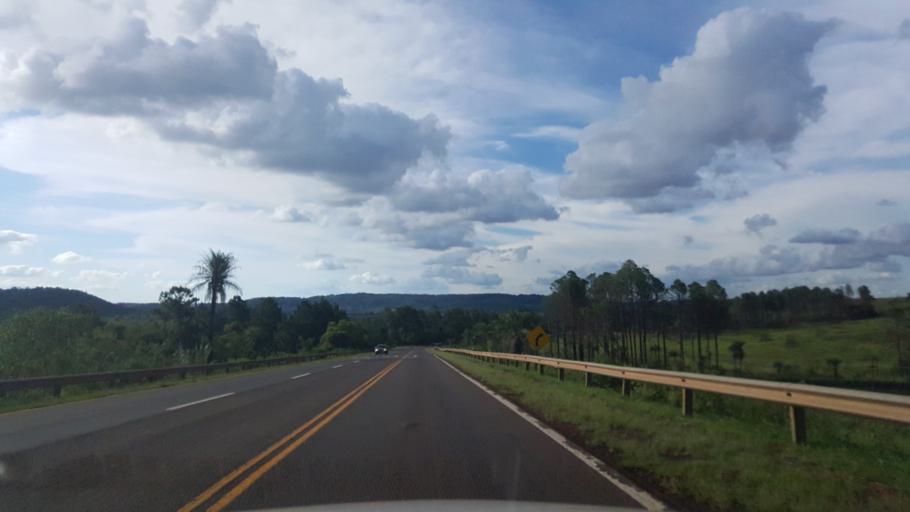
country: AR
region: Misiones
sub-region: Departamento de Candelaria
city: Loreto
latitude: -27.3265
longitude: -55.5430
